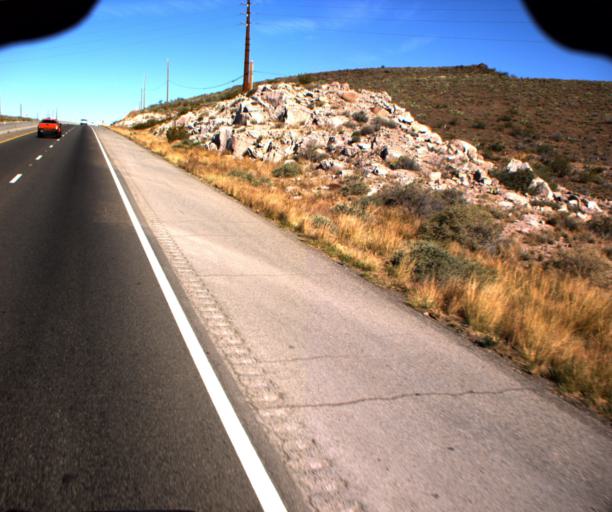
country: US
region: Arizona
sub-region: Mohave County
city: Kingman
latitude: 35.2056
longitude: -114.0934
